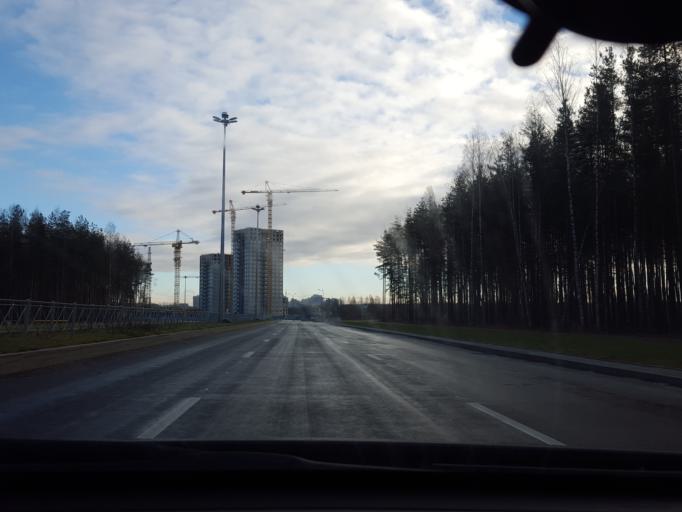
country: RU
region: St.-Petersburg
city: Pargolovo
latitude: 60.0589
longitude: 30.2619
